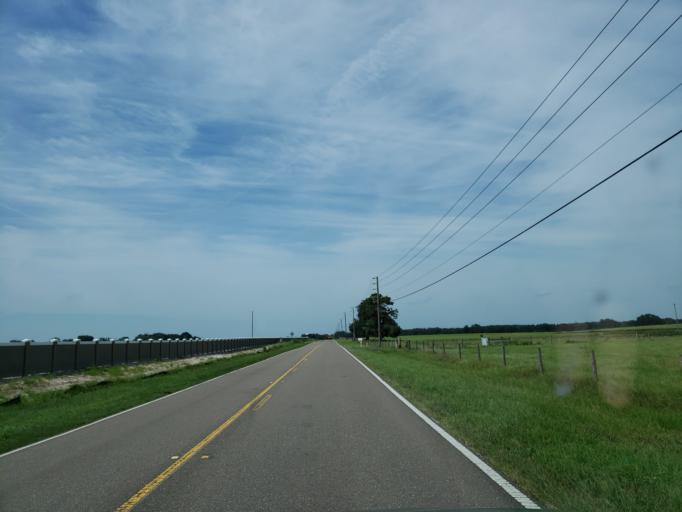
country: US
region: Florida
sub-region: Pasco County
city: San Antonio
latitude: 28.2832
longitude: -82.2786
